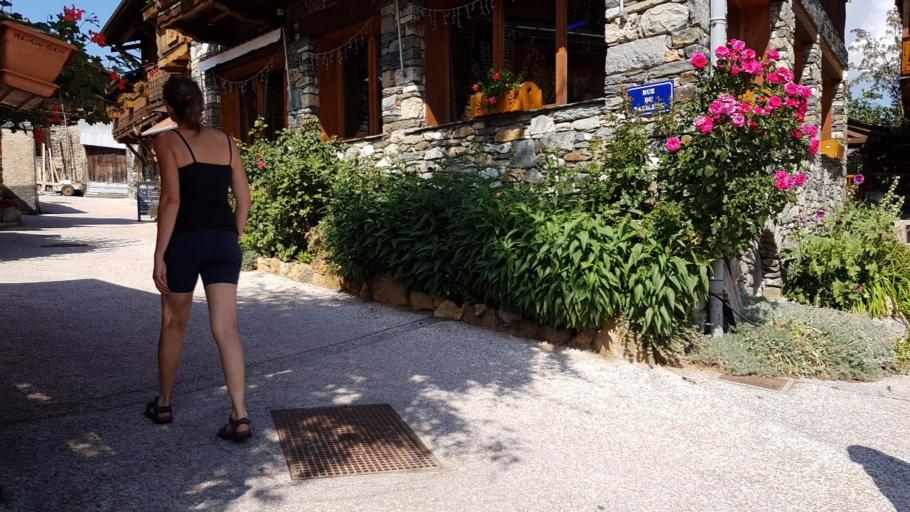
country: FR
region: Rhone-Alpes
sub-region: Departement de la Savoie
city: Belle-Plagne
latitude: 45.5603
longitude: 6.7366
